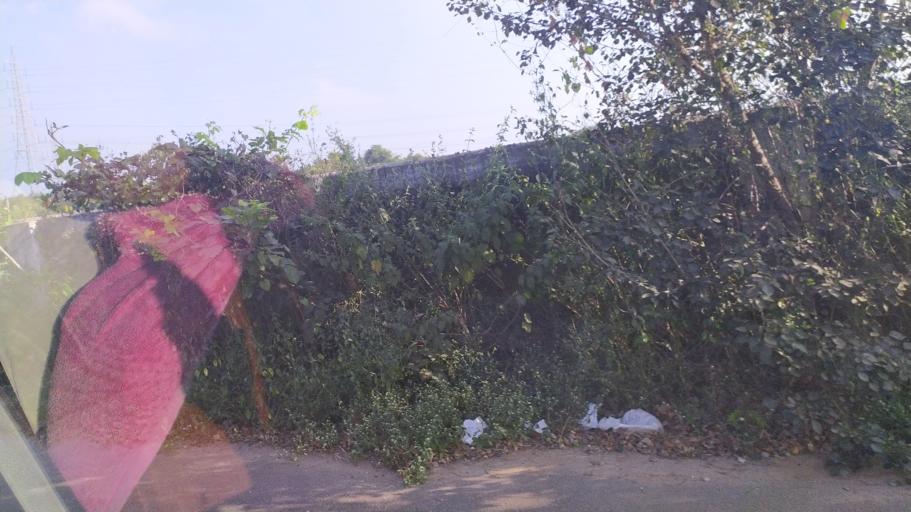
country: IN
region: Telangana
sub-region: Hyderabad
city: Hyderabad
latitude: 17.3284
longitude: 78.4181
